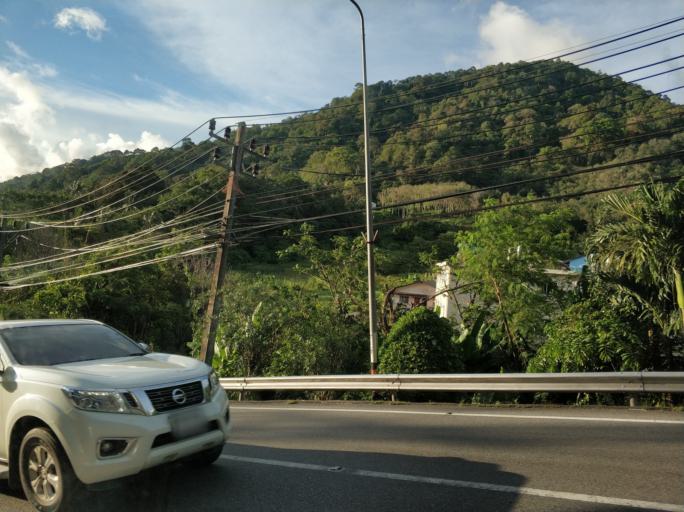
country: TH
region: Phuket
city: Kathu
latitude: 7.9030
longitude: 98.3166
